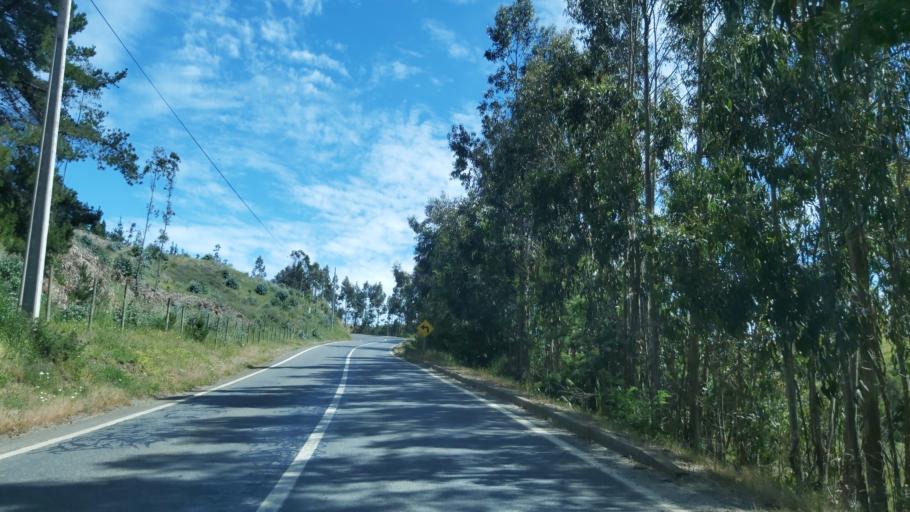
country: CL
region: Maule
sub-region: Provincia de Talca
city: Constitucion
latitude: -35.5689
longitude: -72.6031
